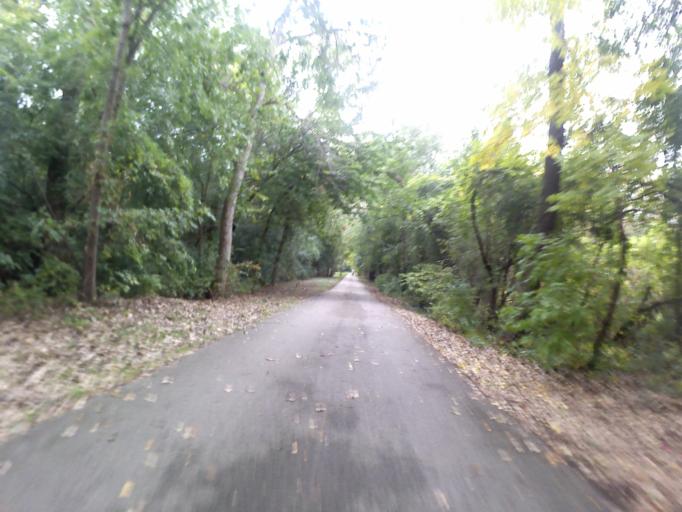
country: US
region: Illinois
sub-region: Kane County
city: Aurora
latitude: 41.7741
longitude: -88.3112
